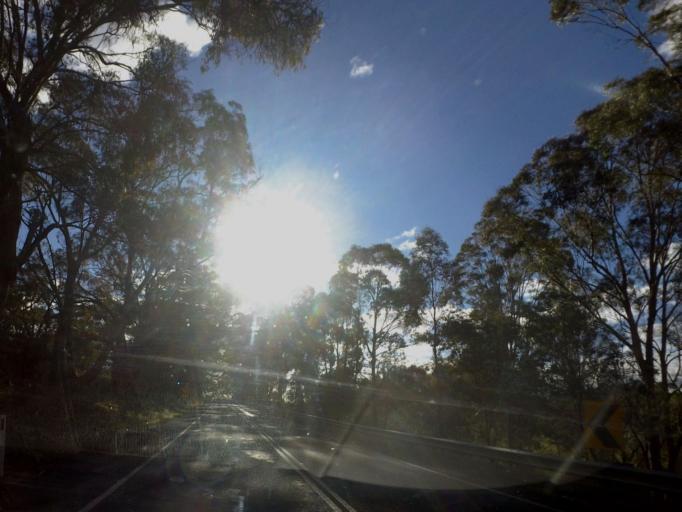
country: AU
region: Victoria
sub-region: Mount Alexander
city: Castlemaine
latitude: -37.1009
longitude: 144.2956
